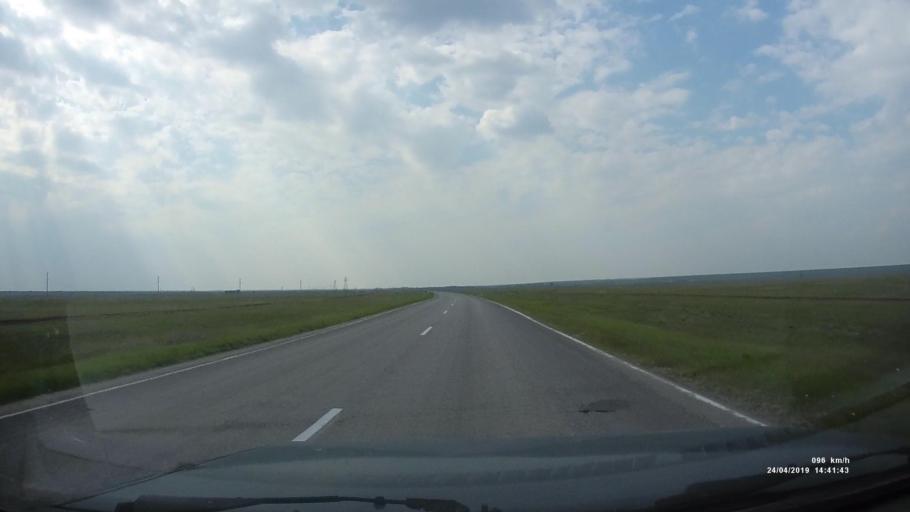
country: RU
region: Rostov
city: Remontnoye
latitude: 46.4476
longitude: 43.8751
